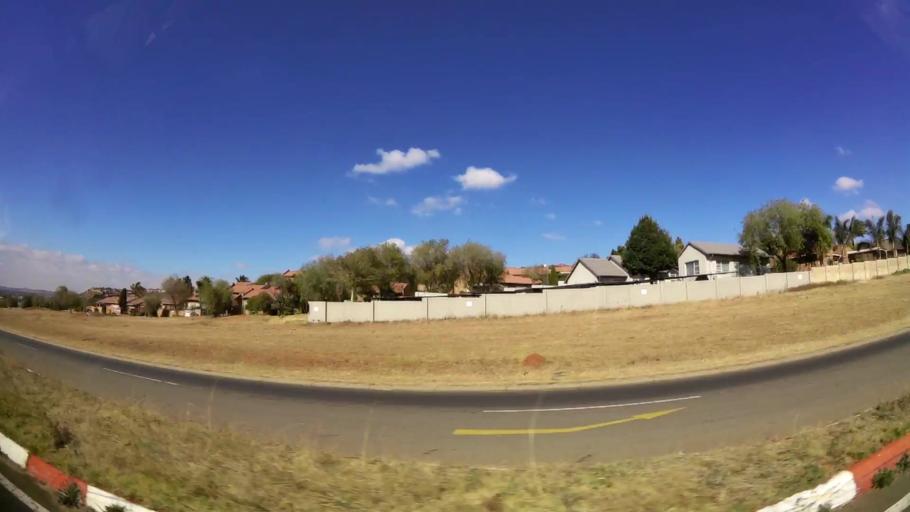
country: ZA
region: Gauteng
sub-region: West Rand District Municipality
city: Krugersdorp
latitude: -26.0870
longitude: 27.8137
